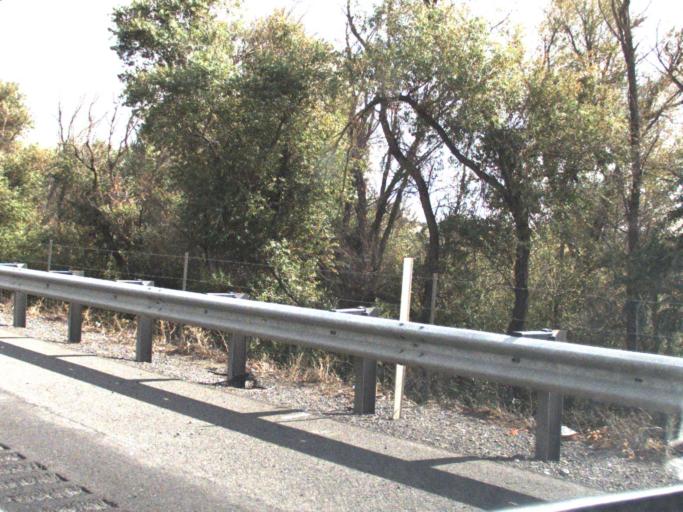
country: US
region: Washington
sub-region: Yakima County
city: Union Gap
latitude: 46.5201
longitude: -120.4639
